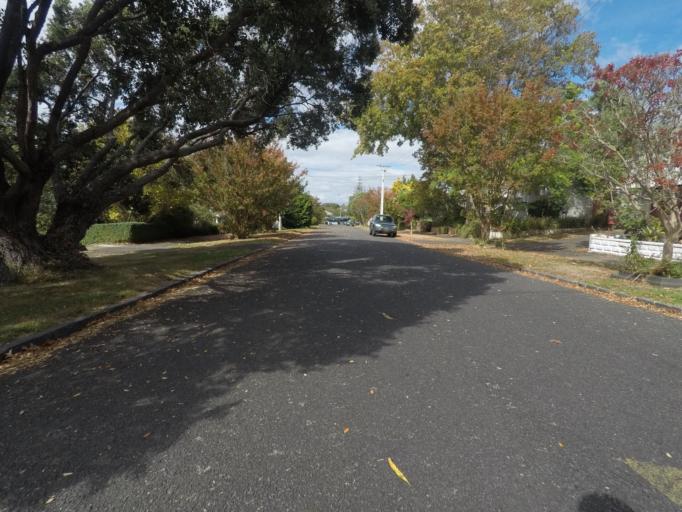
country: NZ
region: Auckland
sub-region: Auckland
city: Auckland
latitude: -36.8806
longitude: 174.7207
